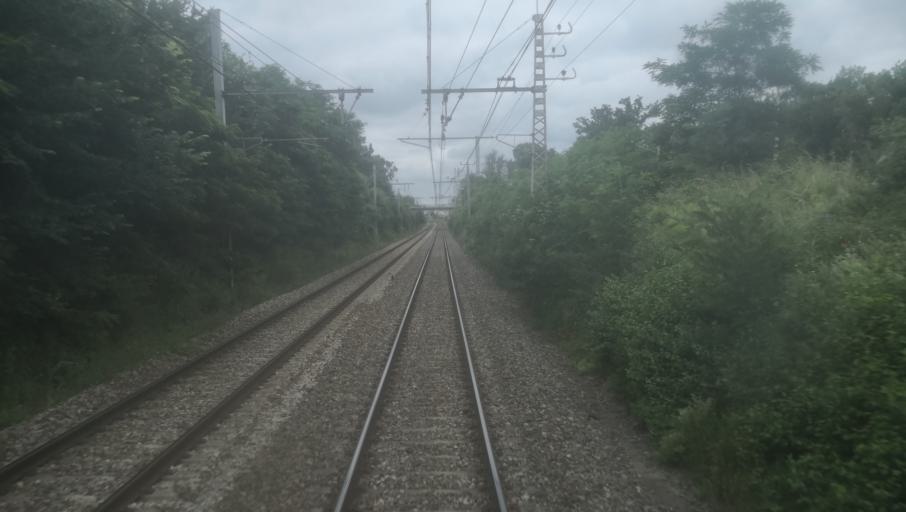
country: FR
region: Midi-Pyrenees
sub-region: Departement de la Haute-Garonne
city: Saint-Orens-de-Gameville
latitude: 43.5577
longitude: 1.5036
